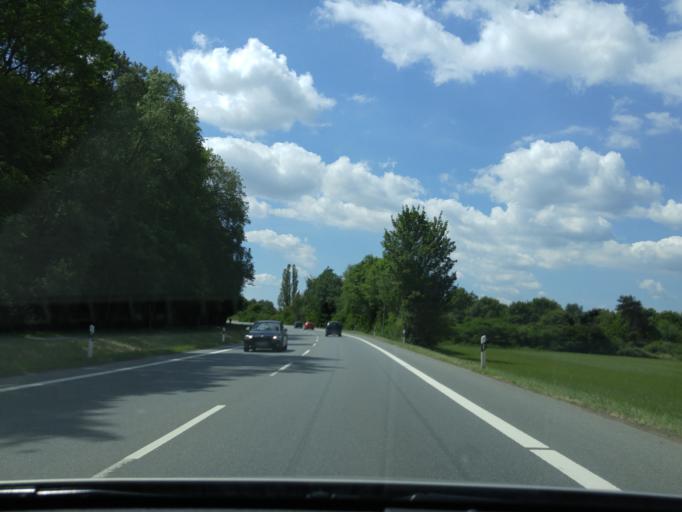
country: DE
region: Hesse
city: Dreieich
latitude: 50.0038
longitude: 8.6835
